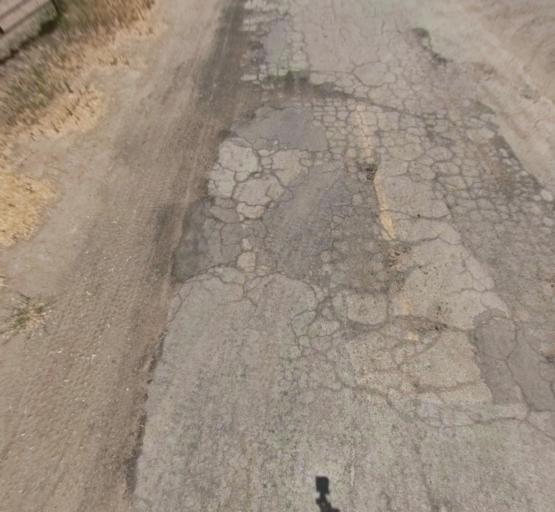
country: US
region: California
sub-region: Madera County
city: Chowchilla
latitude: 37.0959
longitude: -120.3289
